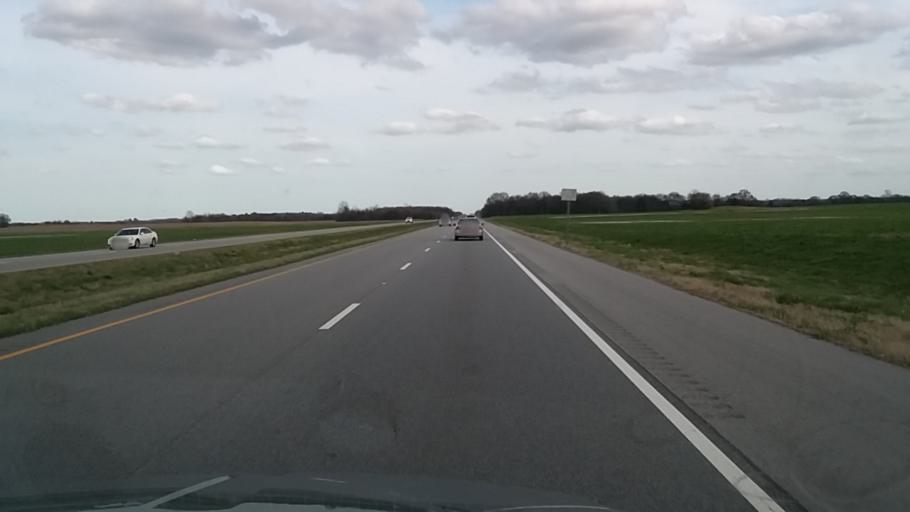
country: US
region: Alabama
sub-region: Lawrence County
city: Town Creek
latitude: 34.6832
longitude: -87.5021
